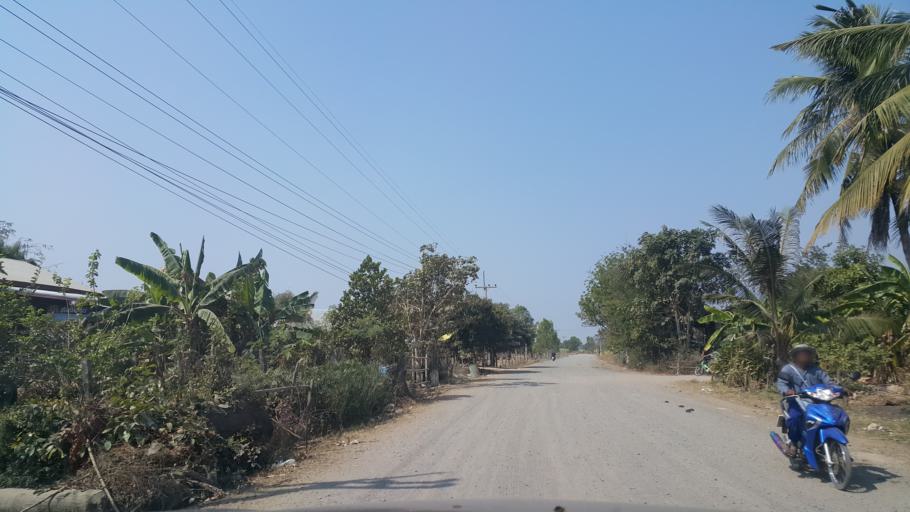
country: TH
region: Buriram
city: Ban Dan
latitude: 15.1324
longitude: 103.3459
